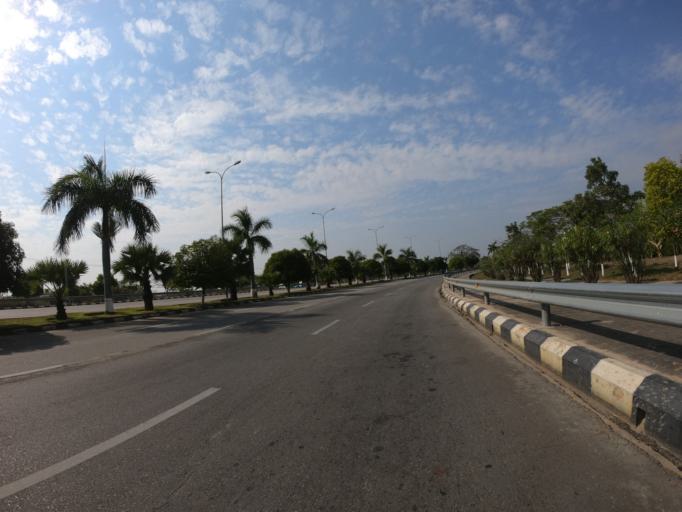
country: MM
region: Mandalay
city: Nay Pyi Taw
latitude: 19.6640
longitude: 96.1210
